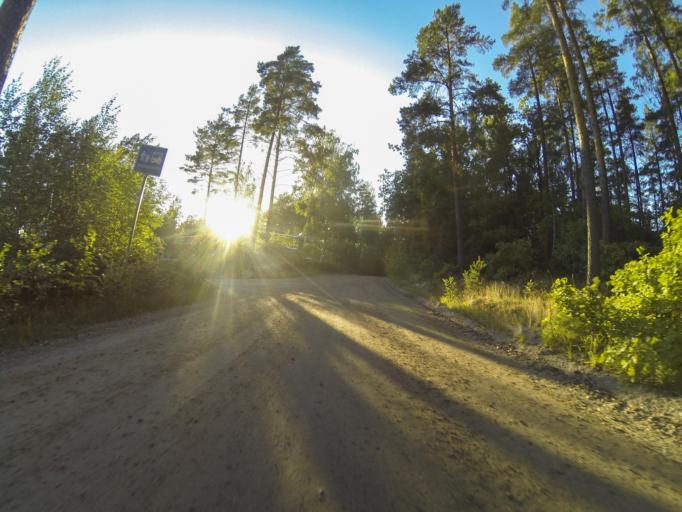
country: SE
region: Vaestmanland
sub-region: Vasteras
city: Vasteras
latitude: 59.5535
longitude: 16.6694
